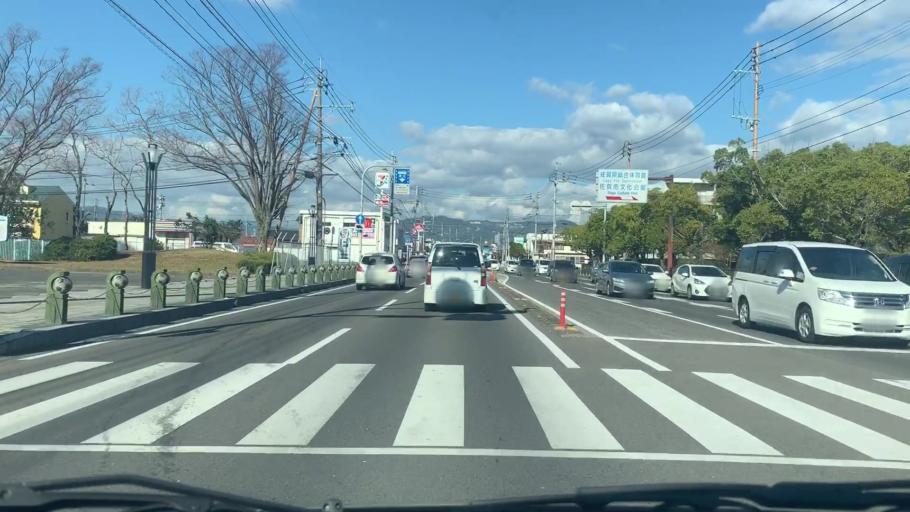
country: JP
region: Saga Prefecture
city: Saga-shi
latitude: 33.2776
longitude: 130.2929
